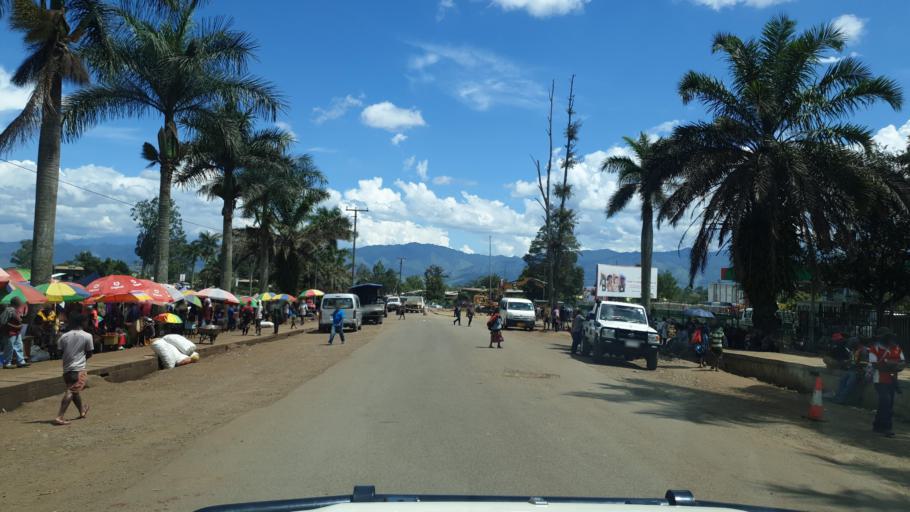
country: PG
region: Eastern Highlands
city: Goroka
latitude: -6.0741
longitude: 145.3899
